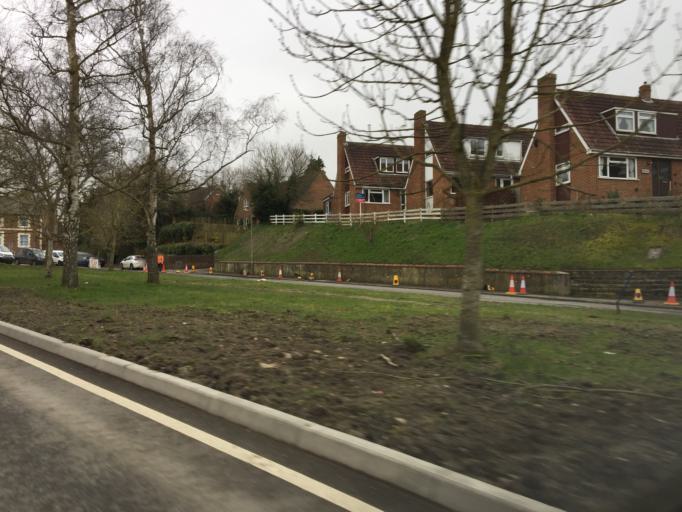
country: GB
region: England
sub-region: Oxfordshire
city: Wantage
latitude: 51.5900
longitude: -1.4522
